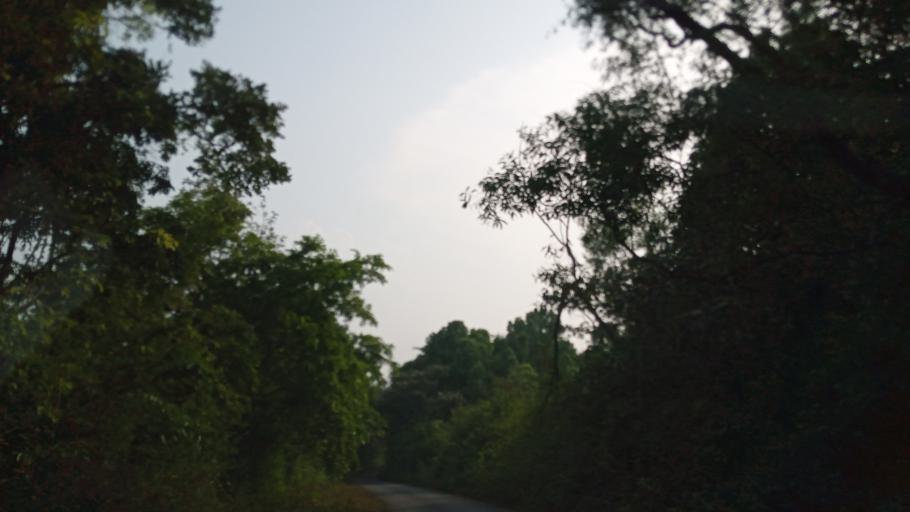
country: IN
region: Karnataka
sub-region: Chikmagalur
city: Mudigere
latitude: 13.0066
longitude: 75.6283
